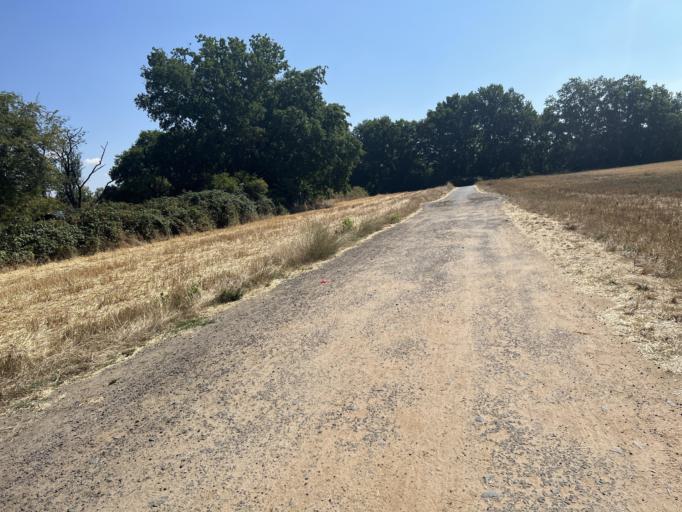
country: DE
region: Hesse
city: Heusenstamm
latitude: 50.0800
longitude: 8.8056
